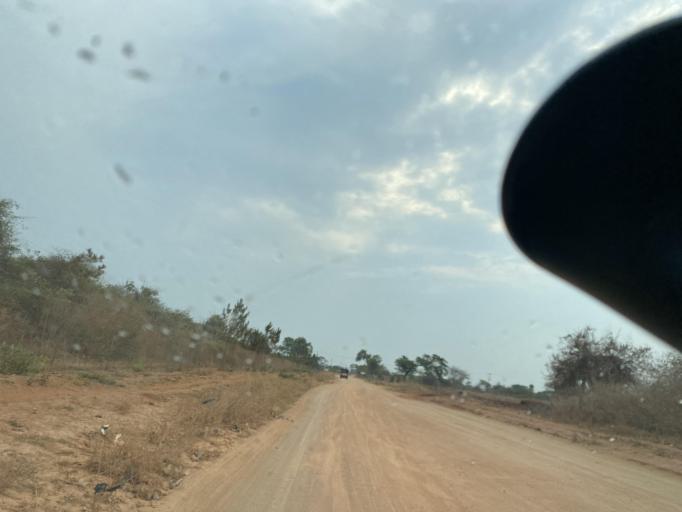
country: ZM
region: Lusaka
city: Lusaka
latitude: -15.2875
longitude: 28.2905
